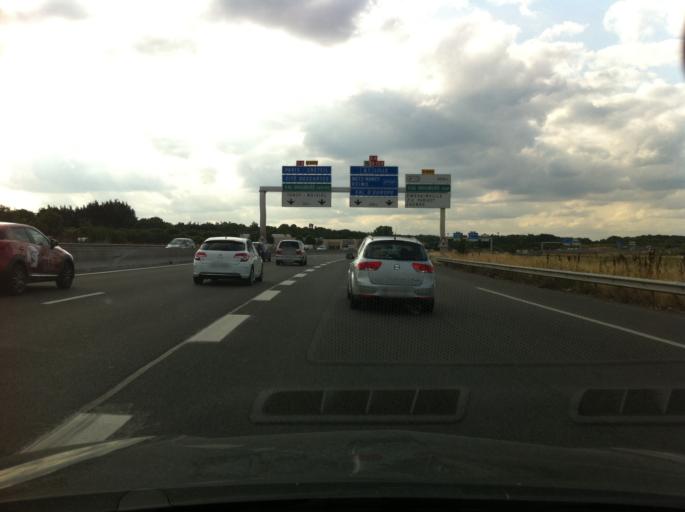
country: FR
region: Ile-de-France
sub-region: Departement de Seine-et-Marne
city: Emerainville
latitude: 48.8168
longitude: 2.6211
